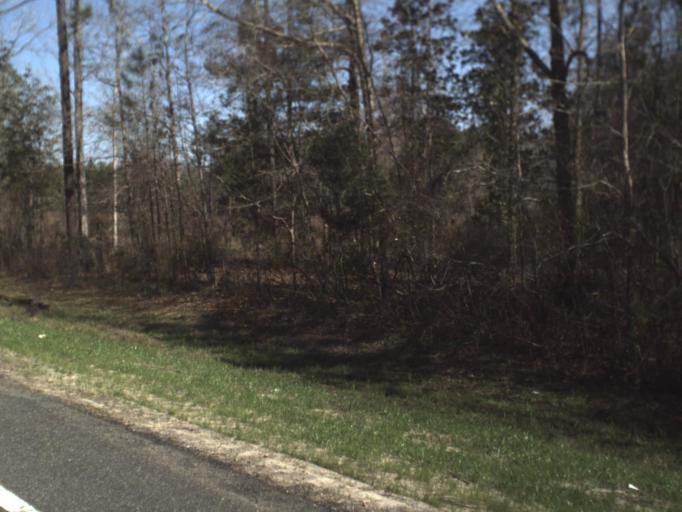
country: US
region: Florida
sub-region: Calhoun County
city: Blountstown
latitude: 30.4276
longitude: -85.0619
